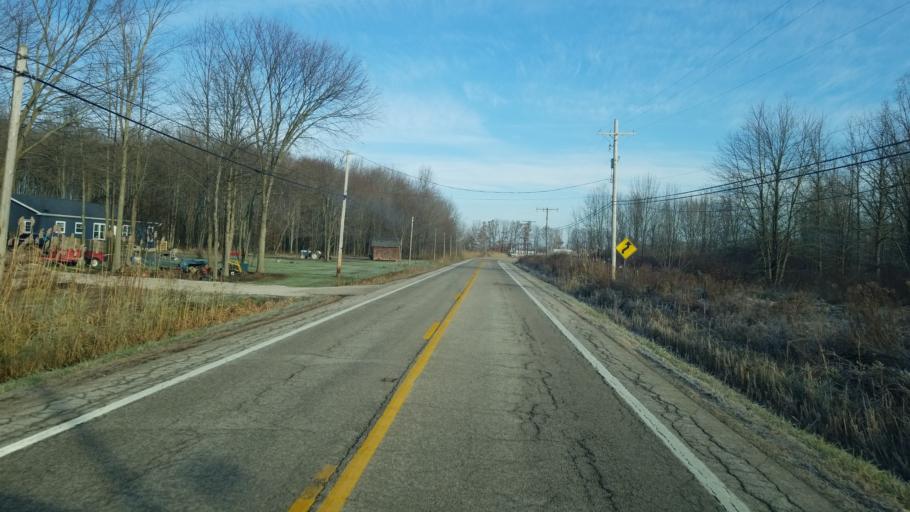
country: US
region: Ohio
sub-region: Ashtabula County
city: Jefferson
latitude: 41.7266
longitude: -80.6691
